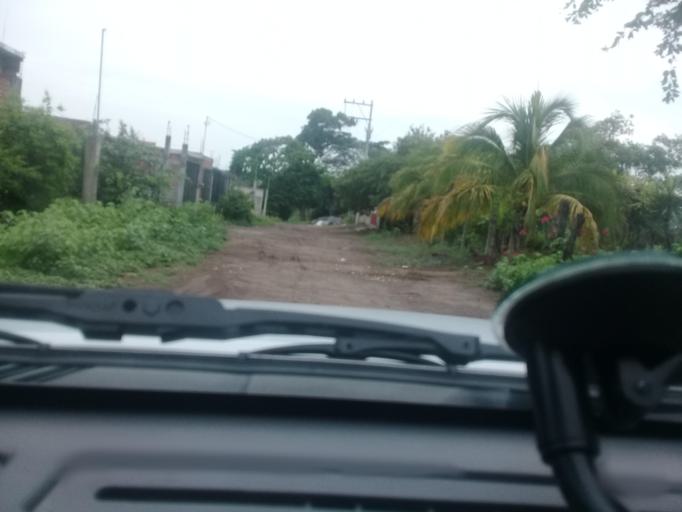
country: MX
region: Veracruz
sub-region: Puente Nacional
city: Cabezas
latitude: 19.3755
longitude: -96.3853
